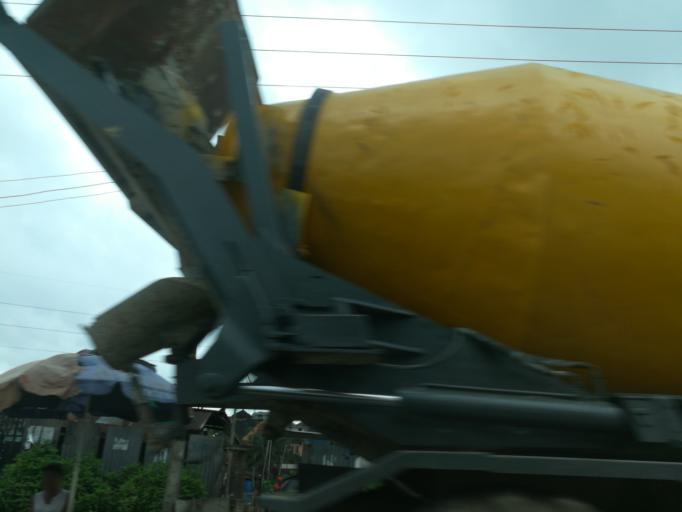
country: NG
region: Rivers
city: Port Harcourt
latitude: 4.8410
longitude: 7.0336
